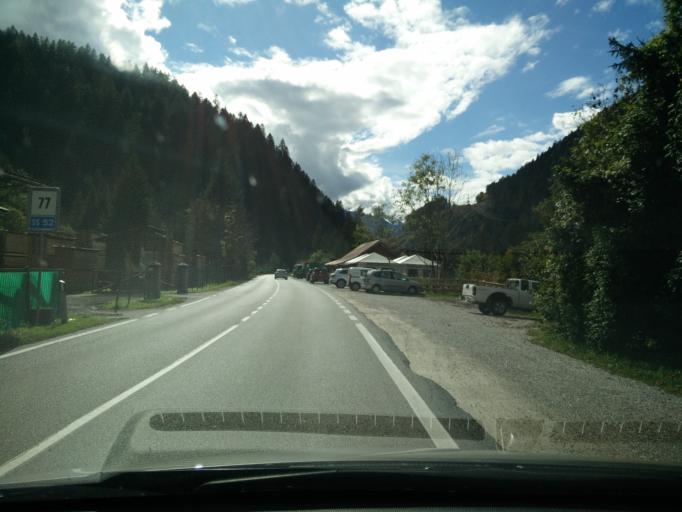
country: IT
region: Veneto
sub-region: Provincia di Belluno
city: Vigo di Cadore
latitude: 46.5001
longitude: 12.4551
